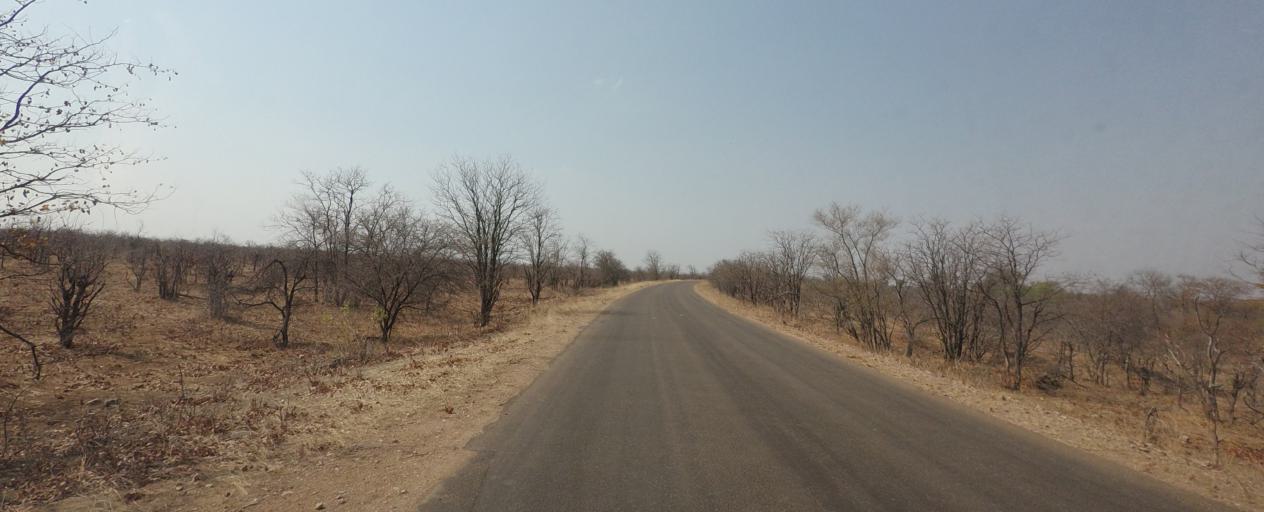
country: ZA
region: Limpopo
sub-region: Mopani District Municipality
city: Giyani
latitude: -23.1836
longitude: 31.3190
